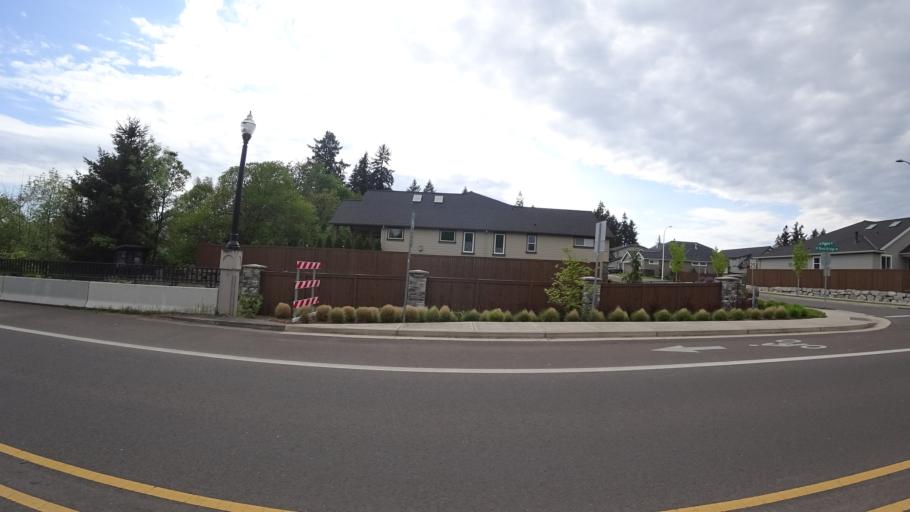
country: US
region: Oregon
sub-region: Washington County
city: Hillsboro
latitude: 45.4909
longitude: -122.9519
